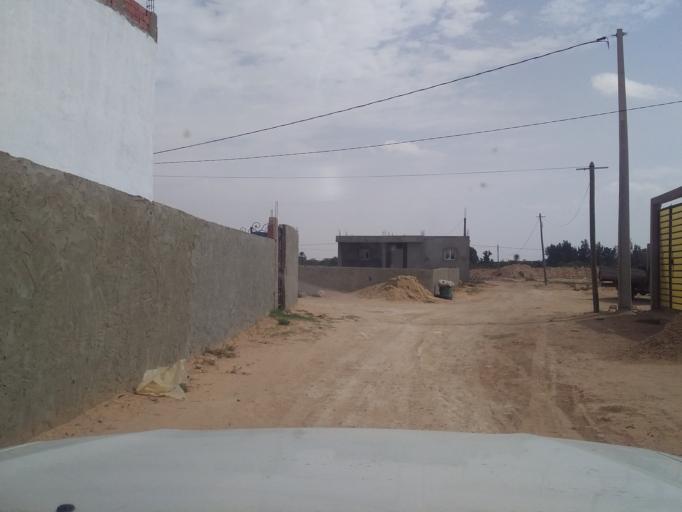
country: TN
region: Qabis
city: Matmata
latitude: 33.6131
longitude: 10.2764
